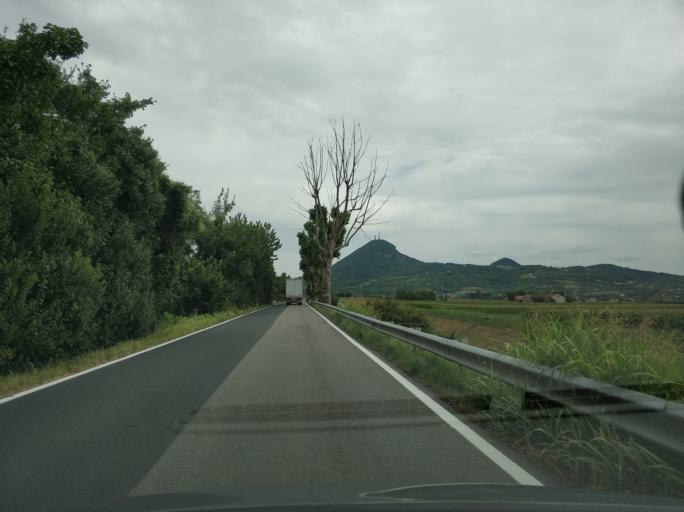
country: IT
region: Veneto
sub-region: Provincia di Padova
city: Lozzo Atestino
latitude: 45.2631
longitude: 11.6224
